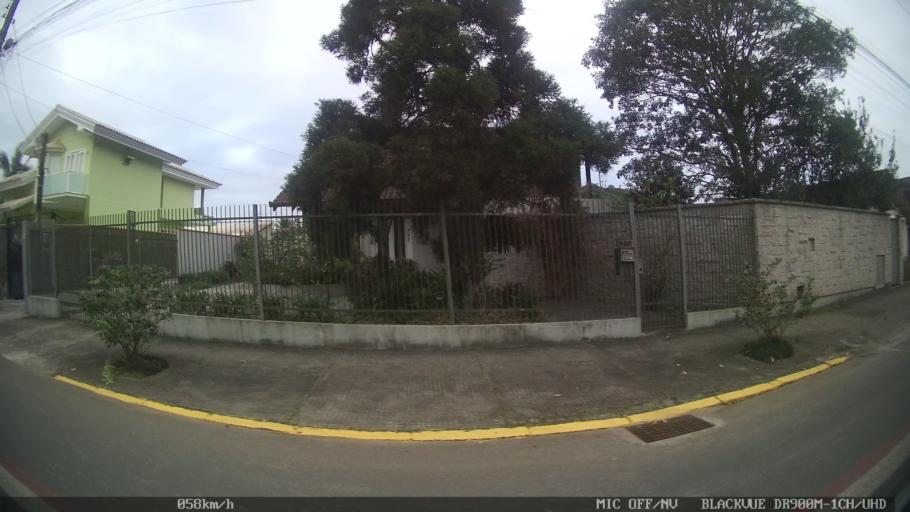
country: BR
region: Santa Catarina
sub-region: Joinville
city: Joinville
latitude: -26.2917
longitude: -48.8538
